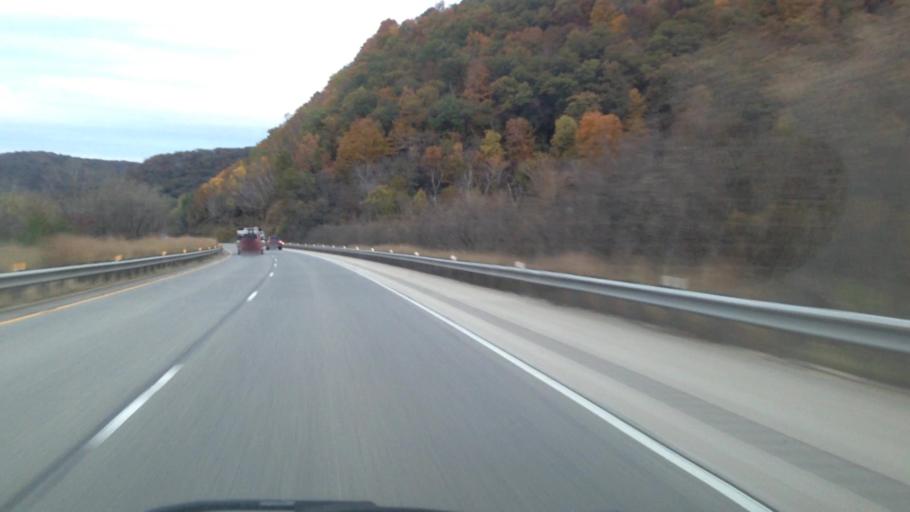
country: US
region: Wisconsin
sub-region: Trempealeau County
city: Trempealeau
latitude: 43.9284
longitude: -91.4125
